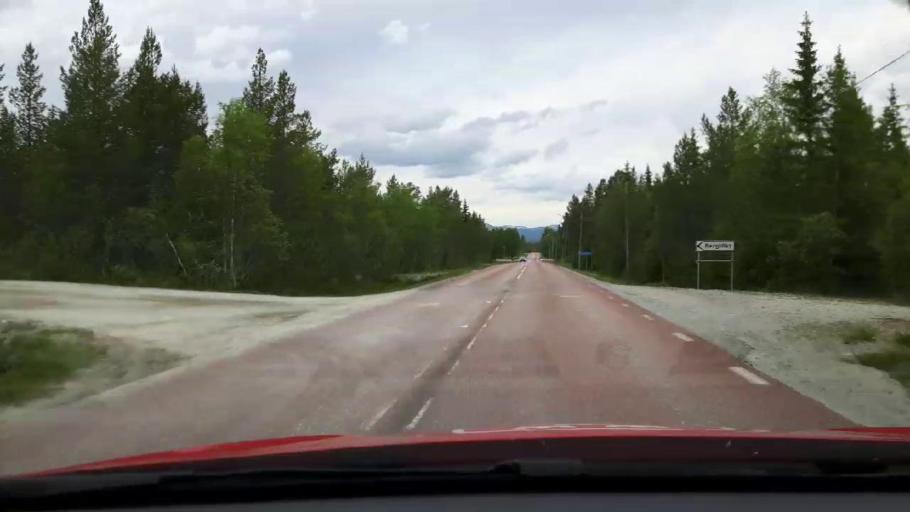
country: NO
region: Hedmark
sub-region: Engerdal
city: Engerdal
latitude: 62.5035
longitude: 12.6223
